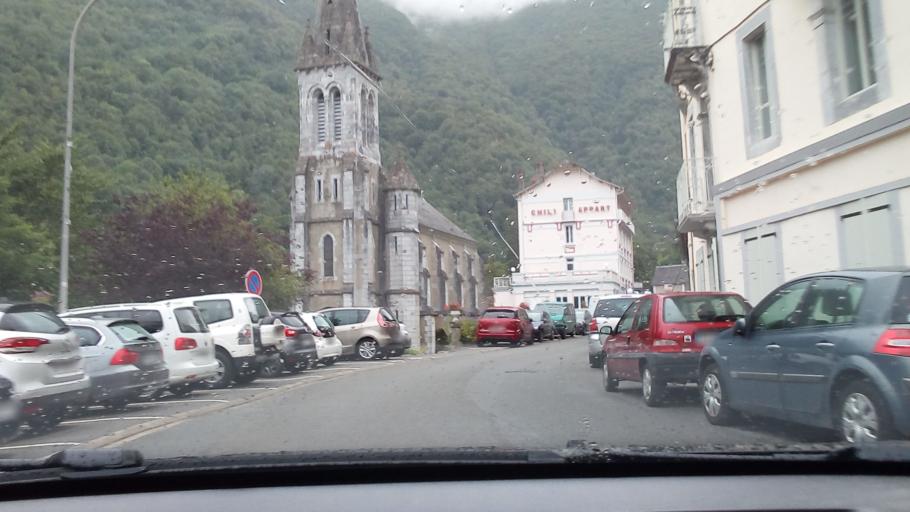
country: FR
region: Midi-Pyrenees
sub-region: Departement des Hautes-Pyrenees
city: Luz-Saint-Sauveur
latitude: 42.8624
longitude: -0.0095
